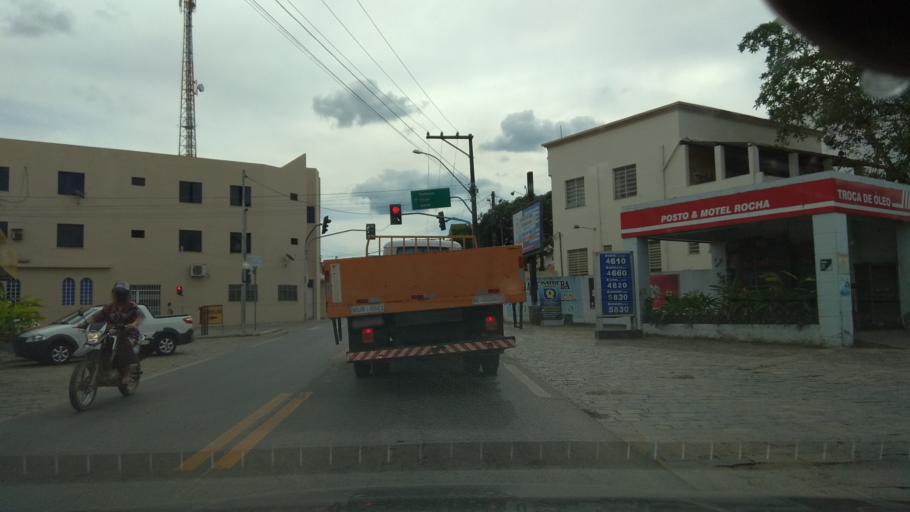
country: BR
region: Bahia
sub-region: Ipiau
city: Ipiau
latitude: -14.1383
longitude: -39.7338
